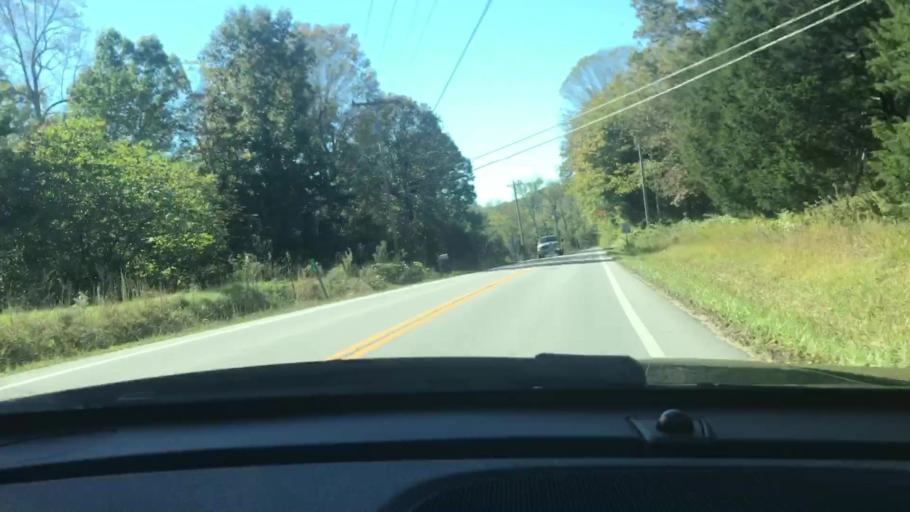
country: US
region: Tennessee
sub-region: Dickson County
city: Charlotte
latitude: 36.1816
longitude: -87.3113
